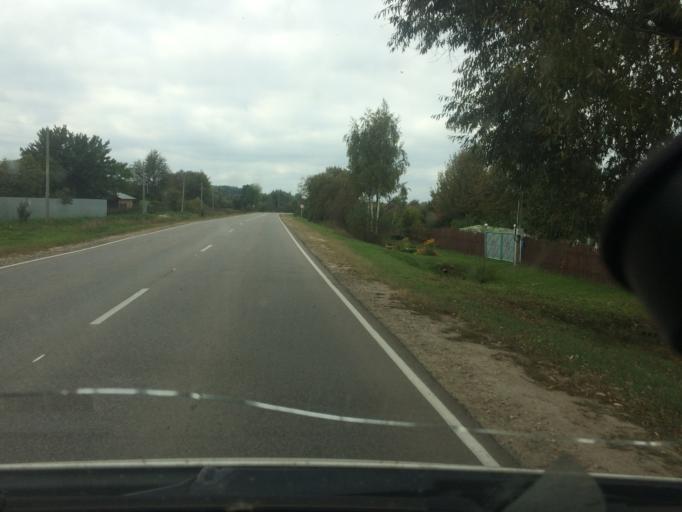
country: RU
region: Tula
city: Odoyev
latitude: 53.9987
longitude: 36.6734
